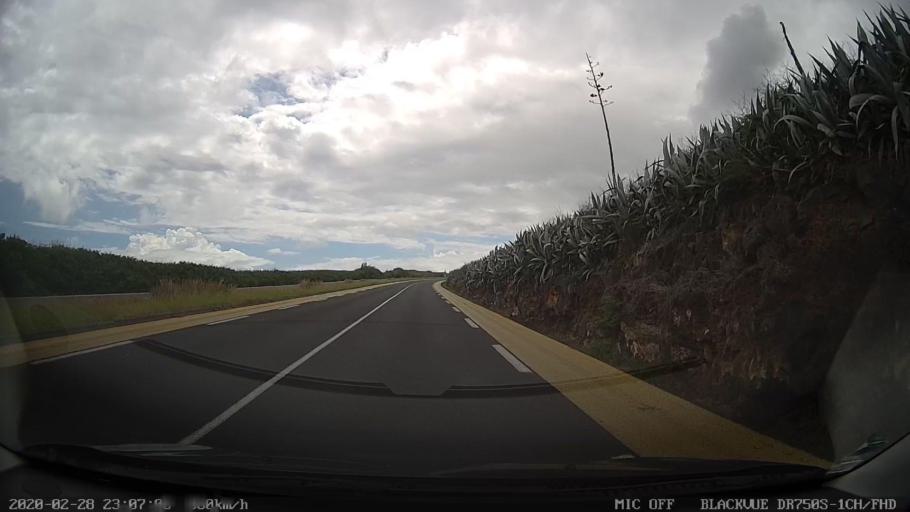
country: RE
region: Reunion
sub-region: Reunion
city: Saint-Leu
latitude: -21.1489
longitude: 55.2748
